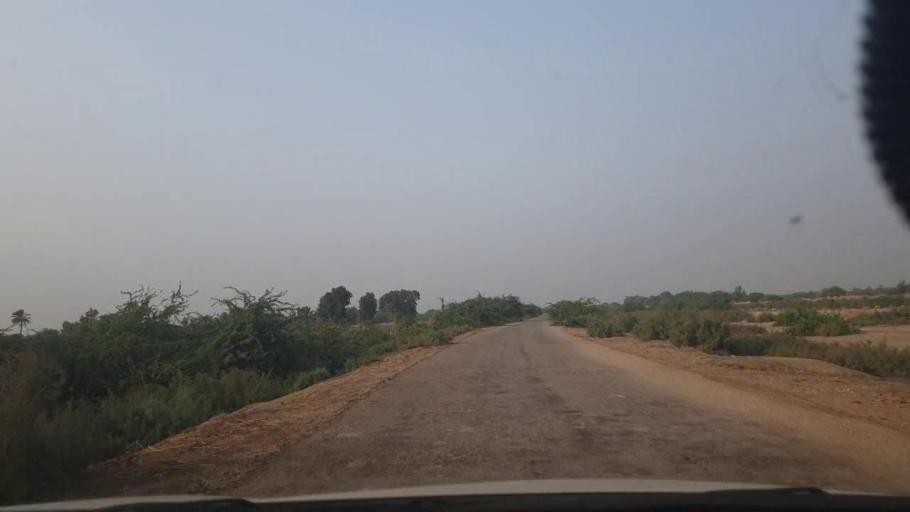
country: PK
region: Sindh
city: Bulri
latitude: 24.8228
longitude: 68.4033
